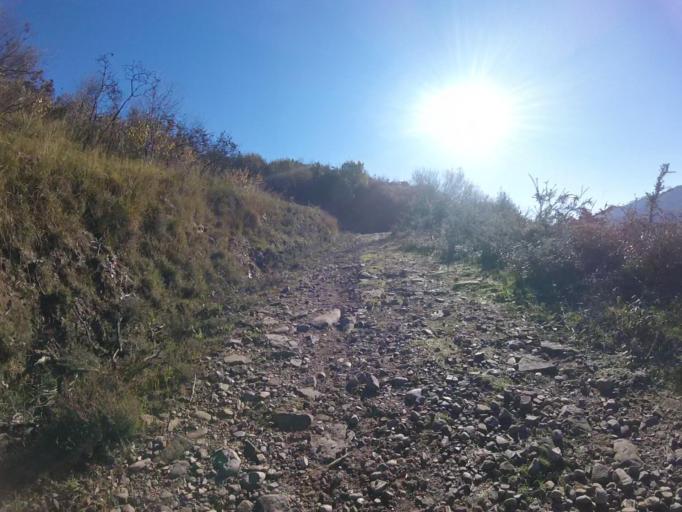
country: FR
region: Aquitaine
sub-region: Departement des Pyrenees-Atlantiques
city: Urrugne
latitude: 43.3274
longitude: -1.7302
